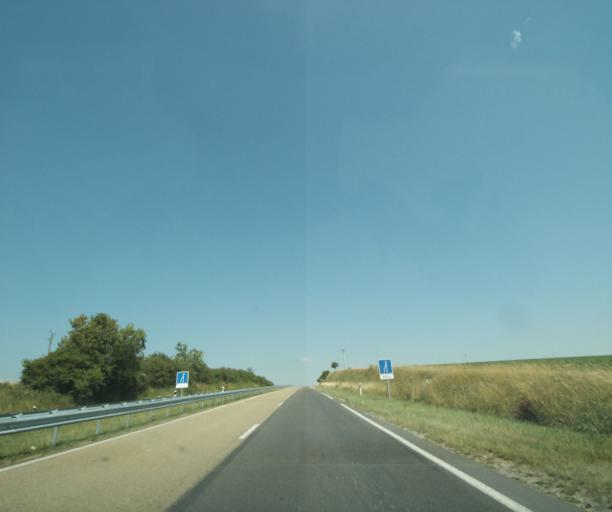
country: FR
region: Champagne-Ardenne
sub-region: Departement de la Marne
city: Fagnieres
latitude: 49.0513
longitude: 4.3034
